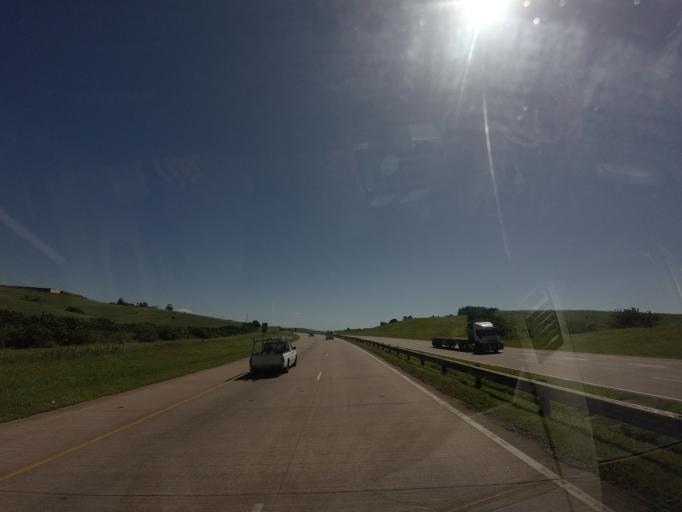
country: ZA
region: KwaZulu-Natal
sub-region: iLembe District Municipality
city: Stanger
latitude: -29.4352
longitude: 31.2691
